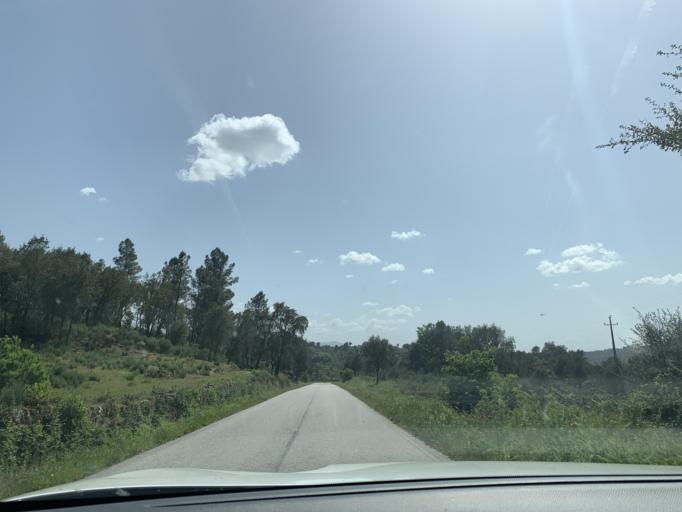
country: PT
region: Guarda
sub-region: Fornos de Algodres
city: Fornos de Algodres
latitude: 40.5732
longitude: -7.5949
